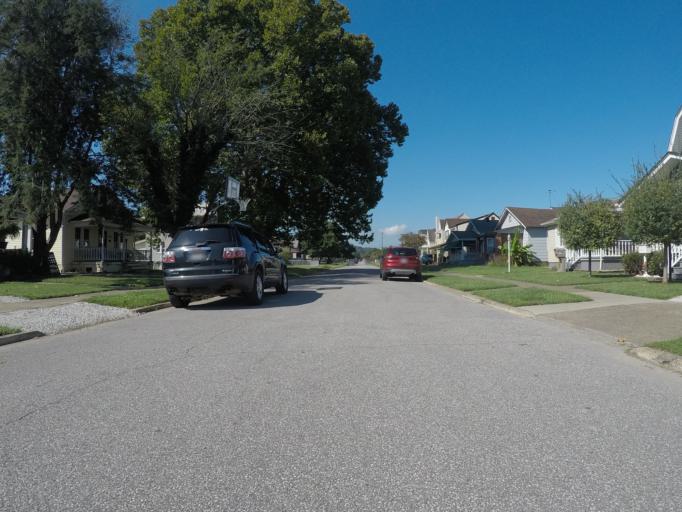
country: US
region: Ohio
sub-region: Lawrence County
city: Burlington
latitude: 38.4015
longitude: -82.5014
